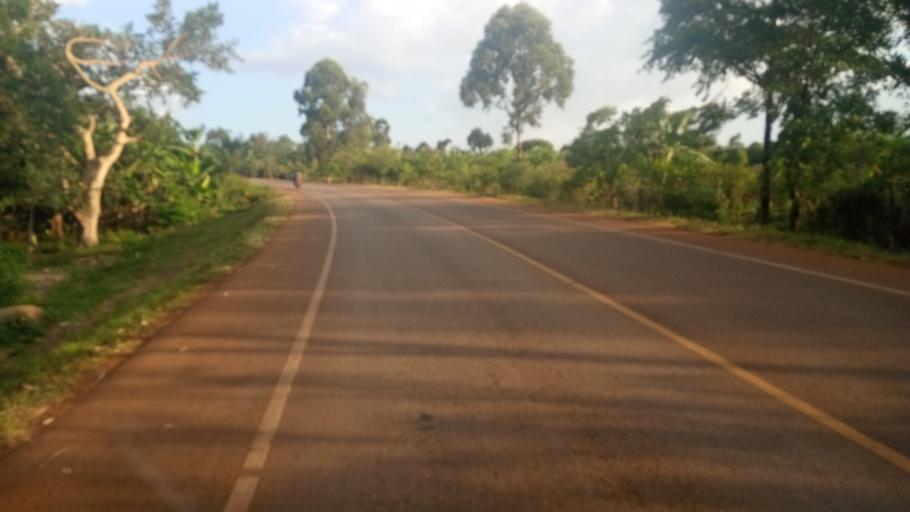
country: UG
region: Eastern Region
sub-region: Sironko District
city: Sironko
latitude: 1.3249
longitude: 34.3303
